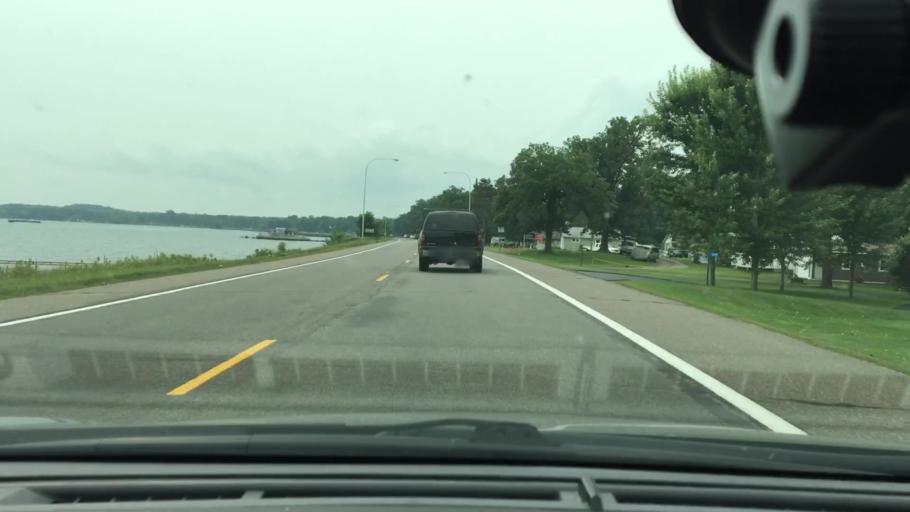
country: US
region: Minnesota
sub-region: Mille Lacs County
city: Vineland
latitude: 46.2676
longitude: -93.8243
